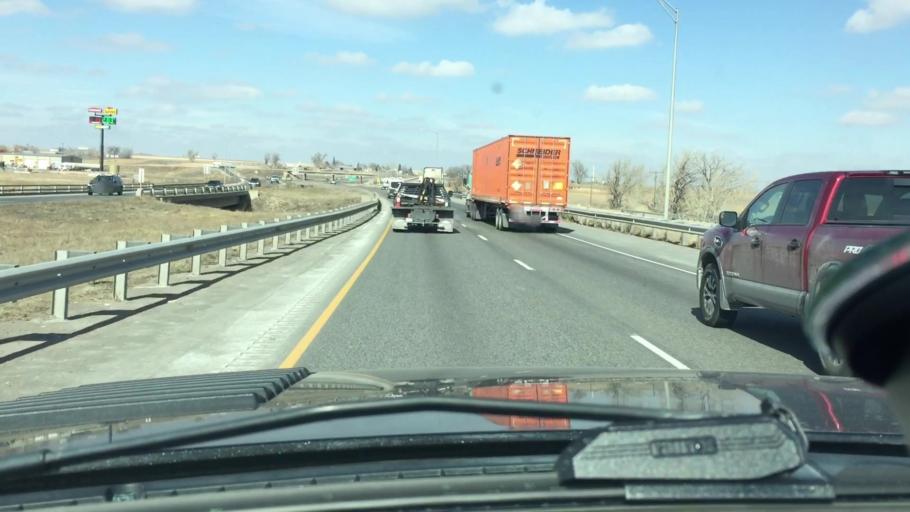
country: US
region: Colorado
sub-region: Weld County
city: Mead
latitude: 40.3001
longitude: -104.9807
